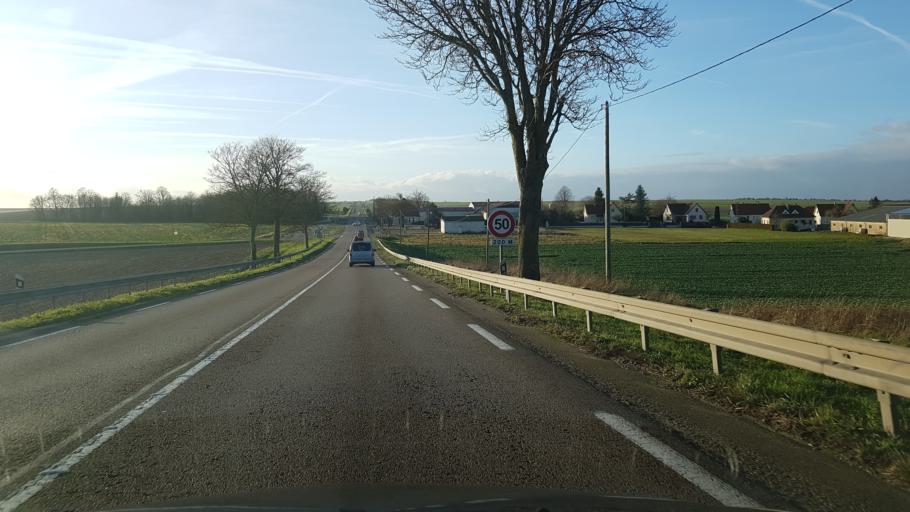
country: FR
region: Champagne-Ardenne
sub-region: Departement de l'Aube
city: Mailly-le-Camp
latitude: 48.7360
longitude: 4.3158
